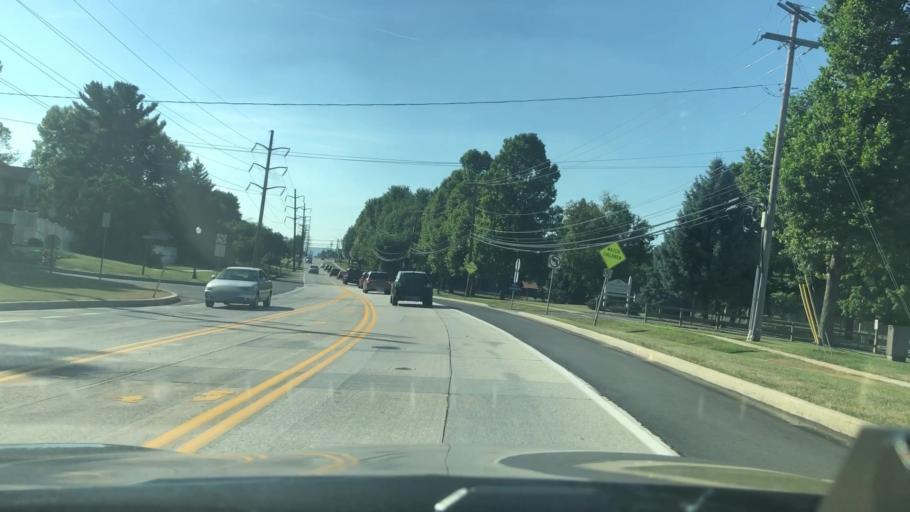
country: US
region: Pennsylvania
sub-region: Cumberland County
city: Shiremanstown
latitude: 40.2138
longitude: -76.9710
